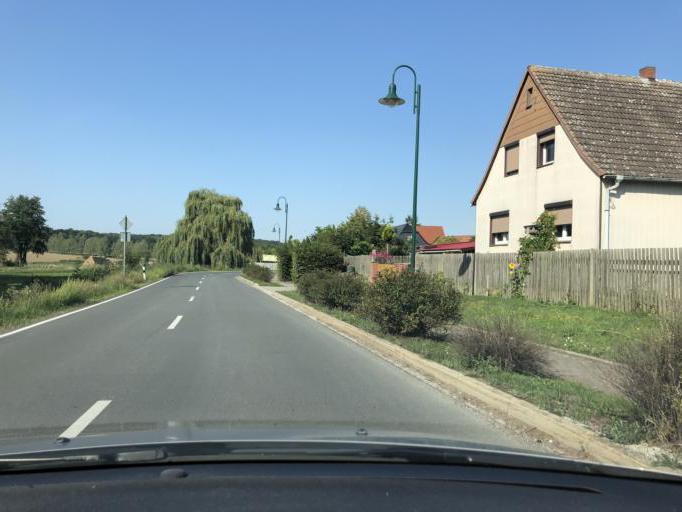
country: DE
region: Thuringia
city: Rastenberg
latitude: 51.1966
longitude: 11.4784
